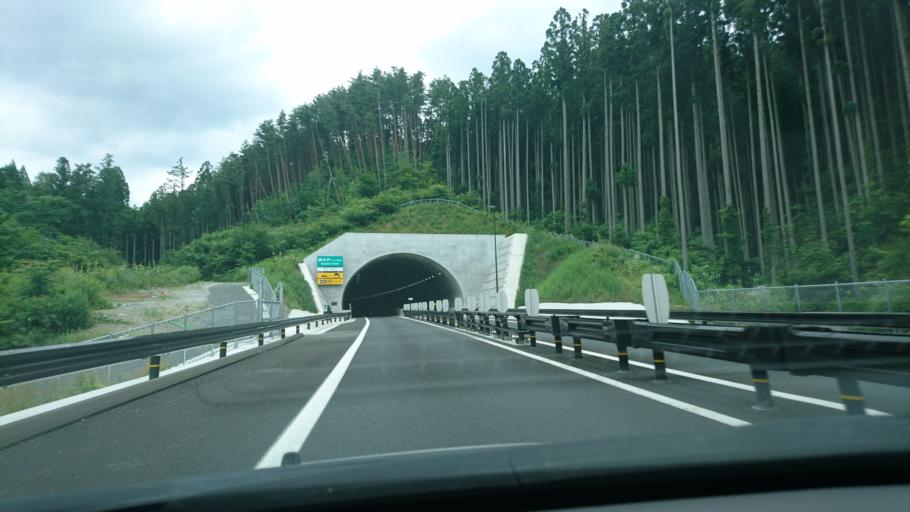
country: JP
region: Iwate
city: Yamada
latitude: 39.4867
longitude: 141.9559
